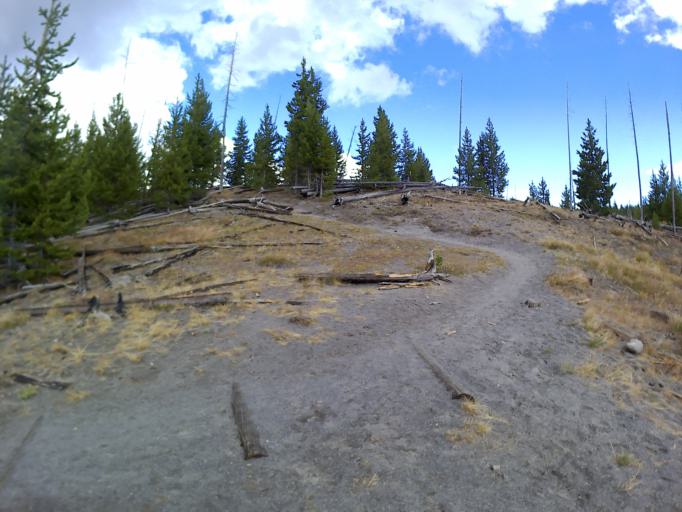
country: US
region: Montana
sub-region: Gallatin County
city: West Yellowstone
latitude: 44.4865
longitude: -110.8748
